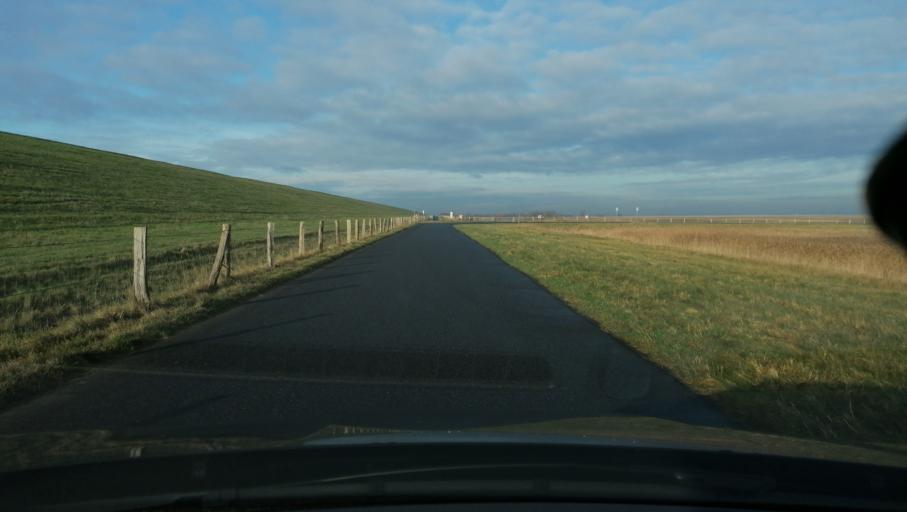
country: DE
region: Schleswig-Holstein
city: Friedrichsgabekoog
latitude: 54.0989
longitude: 8.9475
